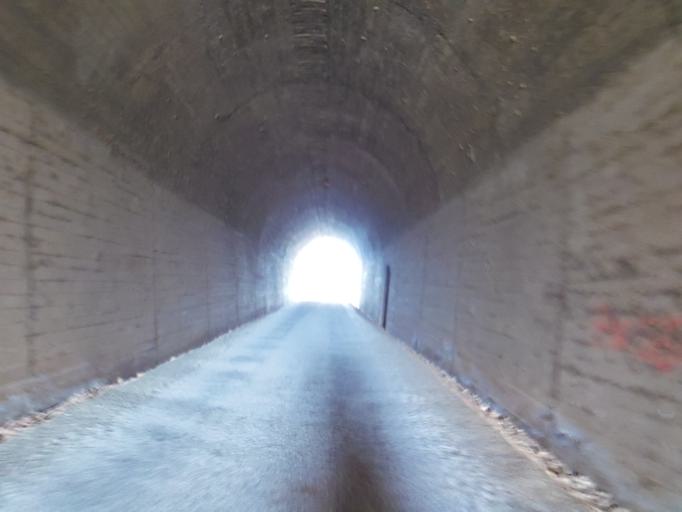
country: ES
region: Castille-La Mancha
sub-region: Provincia de Albacete
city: Robledo
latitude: 38.7789
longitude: -2.3893
